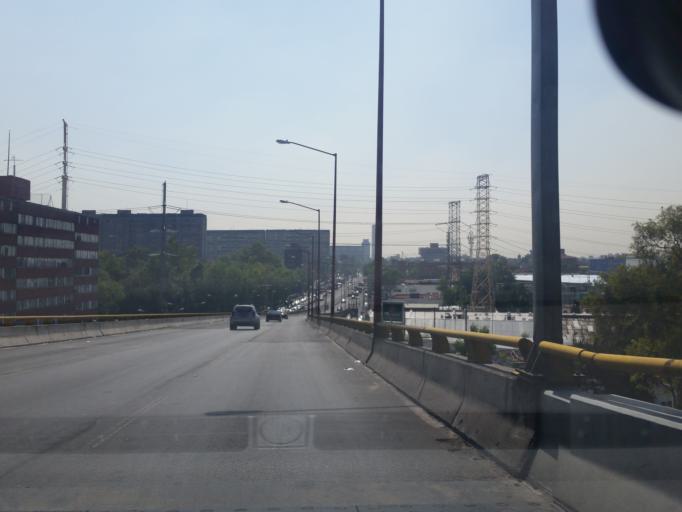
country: MX
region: Mexico City
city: Cuauhtemoc
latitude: 19.4540
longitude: -99.1511
